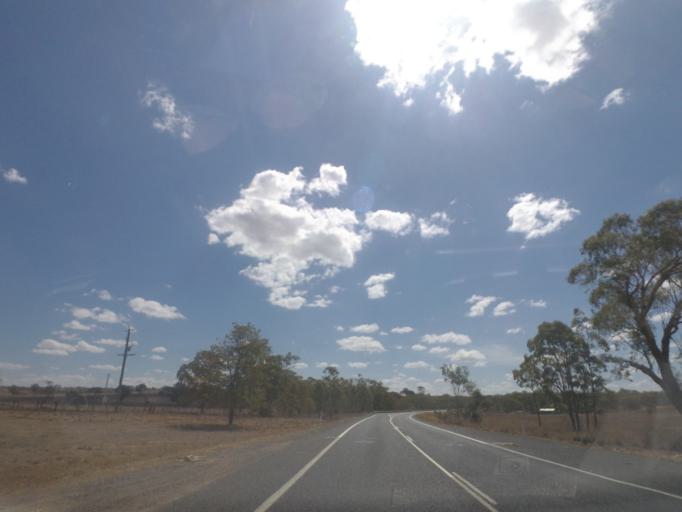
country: AU
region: Queensland
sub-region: Southern Downs
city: Warwick
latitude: -28.1626
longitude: 151.7011
